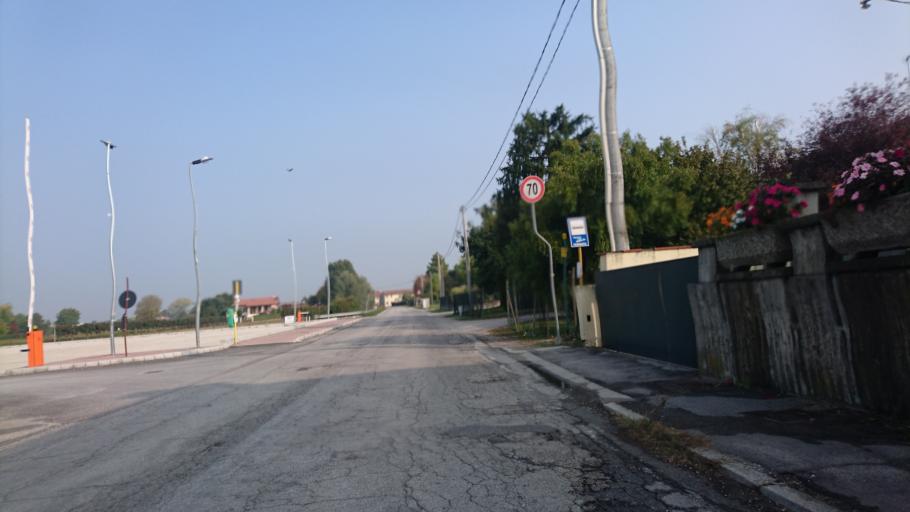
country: IT
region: Veneto
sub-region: Provincia di Padova
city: Curtarolo
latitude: 45.5240
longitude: 11.8432
